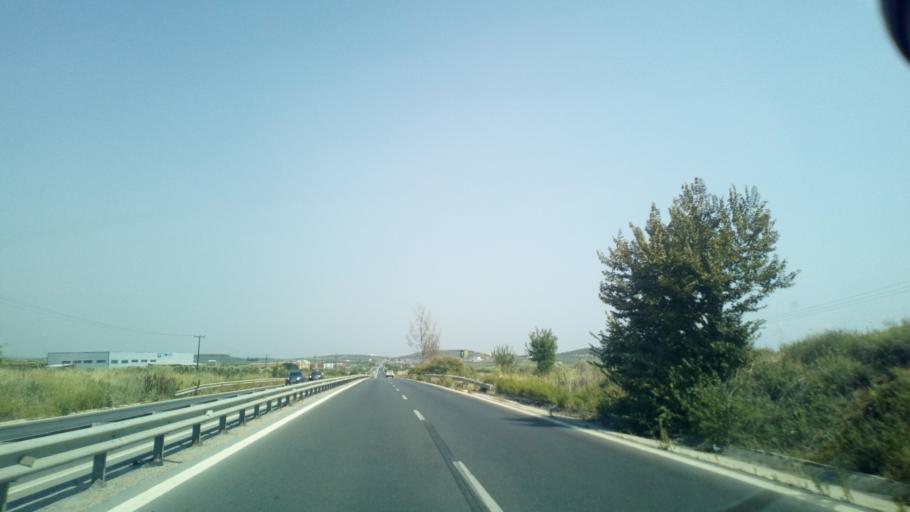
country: GR
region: Central Macedonia
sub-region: Nomos Chalkidikis
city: Nea Flogita
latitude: 40.2638
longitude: 23.2465
